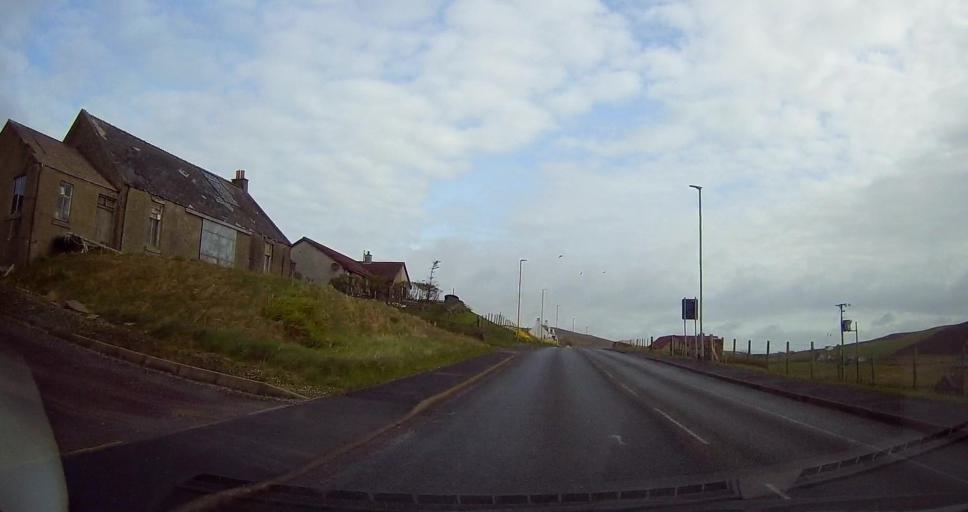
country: GB
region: Scotland
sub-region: Shetland Islands
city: Sandwick
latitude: 60.0477
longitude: -1.2276
